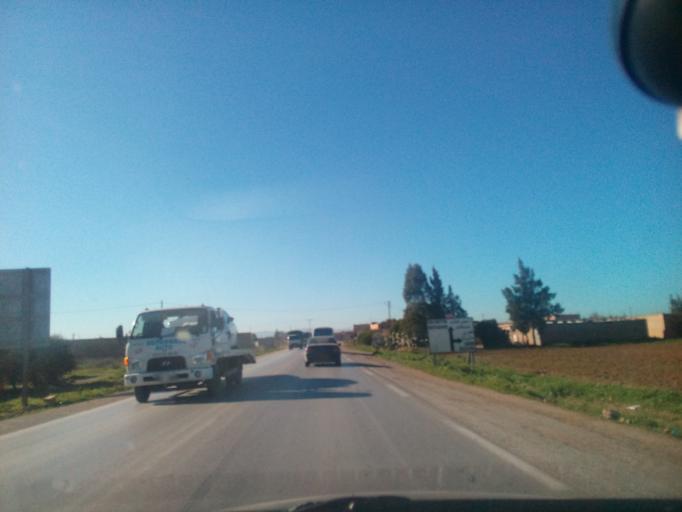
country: DZ
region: Relizane
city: Djidiouia
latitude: 35.8957
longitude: 0.6981
